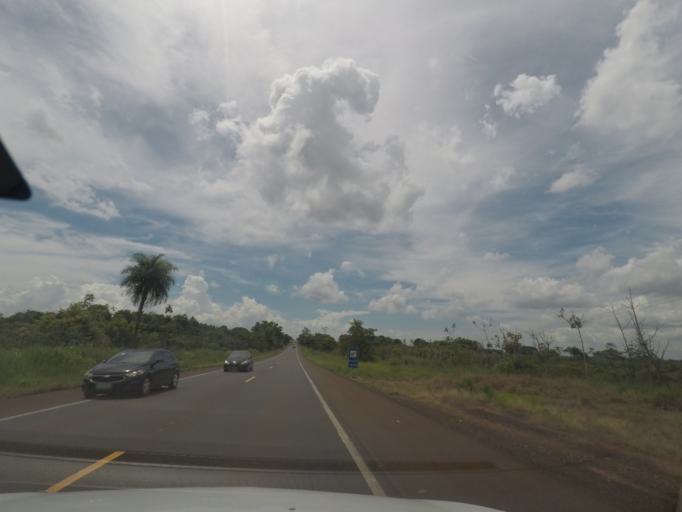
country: BR
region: Sao Paulo
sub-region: Barretos
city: Barretos
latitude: -20.3705
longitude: -48.6456
